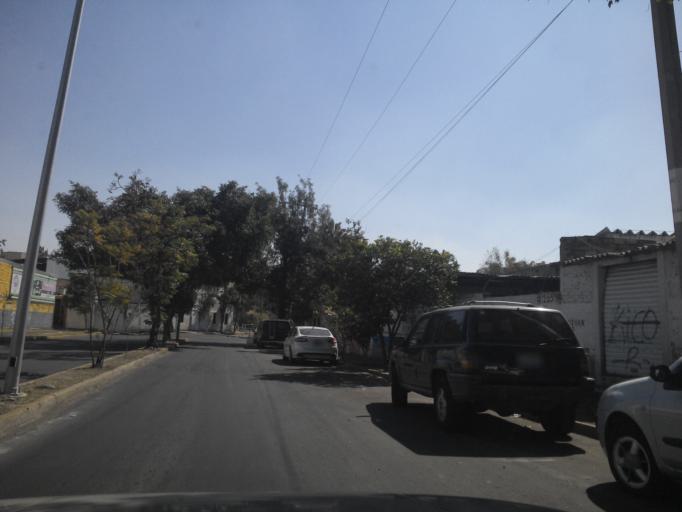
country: MX
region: Jalisco
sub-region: Zapopan
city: Zapopan
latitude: 20.7052
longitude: -103.3586
